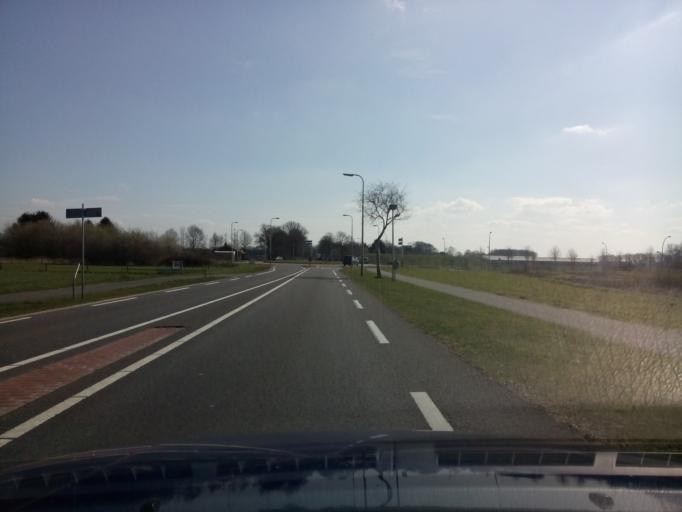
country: NL
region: Drenthe
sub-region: Gemeente Coevorden
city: Coevorden
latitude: 52.6490
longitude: 6.7541
